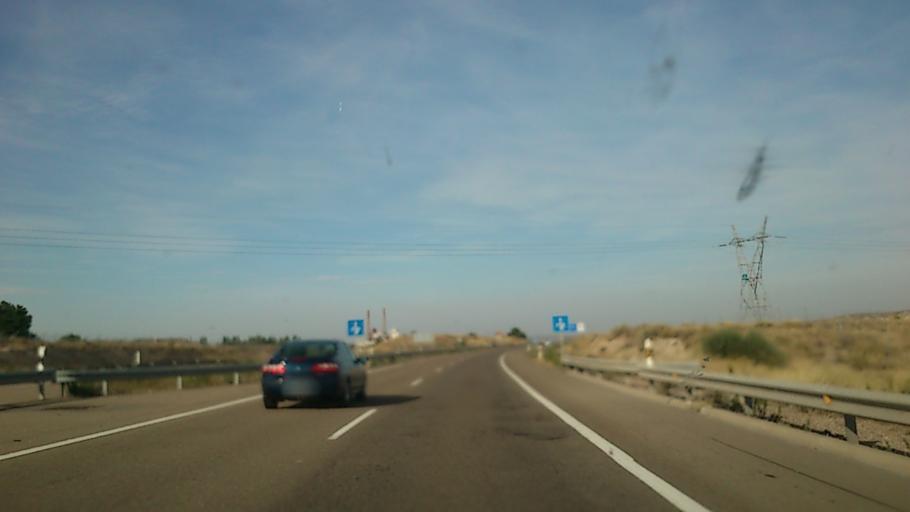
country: ES
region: Aragon
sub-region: Provincia de Zaragoza
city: Cuarte de Huerva
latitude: 41.5869
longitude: -0.9525
